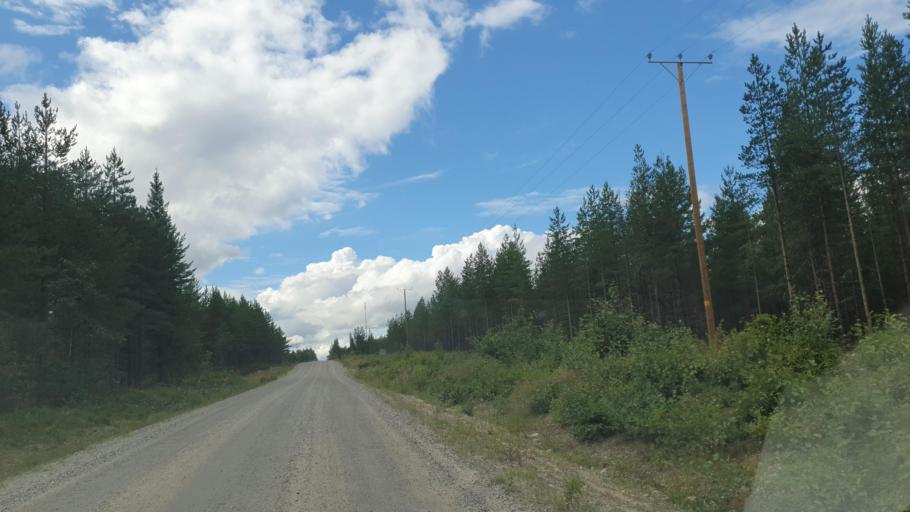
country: FI
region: Kainuu
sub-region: Kehys-Kainuu
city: Kuhmo
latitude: 64.1097
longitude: 29.3578
